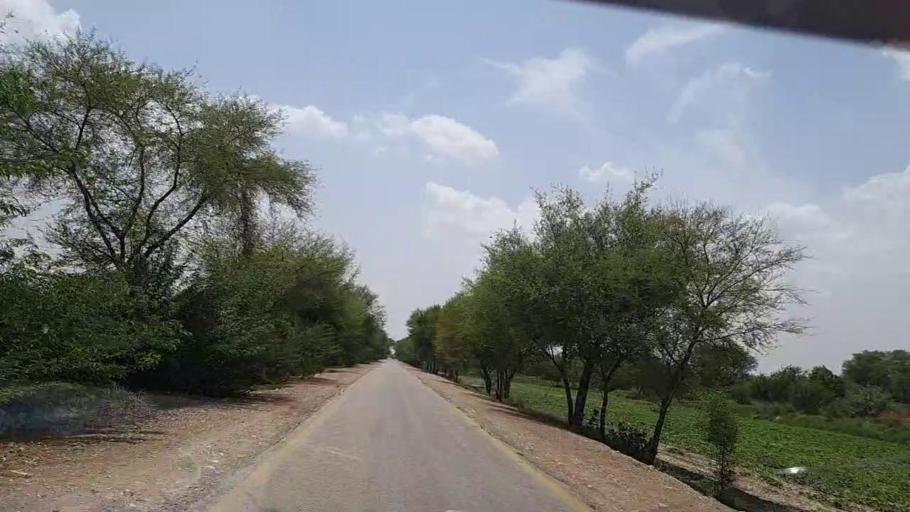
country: PK
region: Sindh
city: Bhan
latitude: 26.5415
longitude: 67.6957
